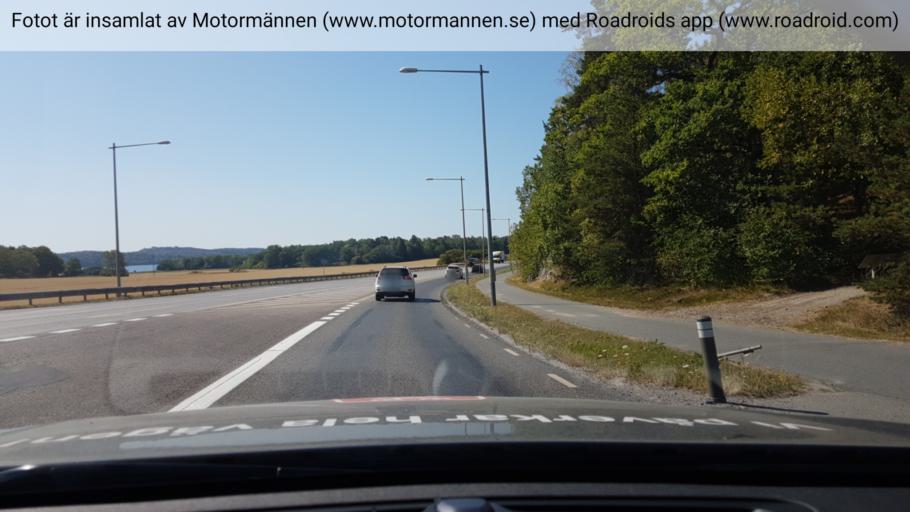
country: SE
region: Stockholm
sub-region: Ekero Kommun
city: Ekeroe
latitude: 59.3101
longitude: 17.8607
